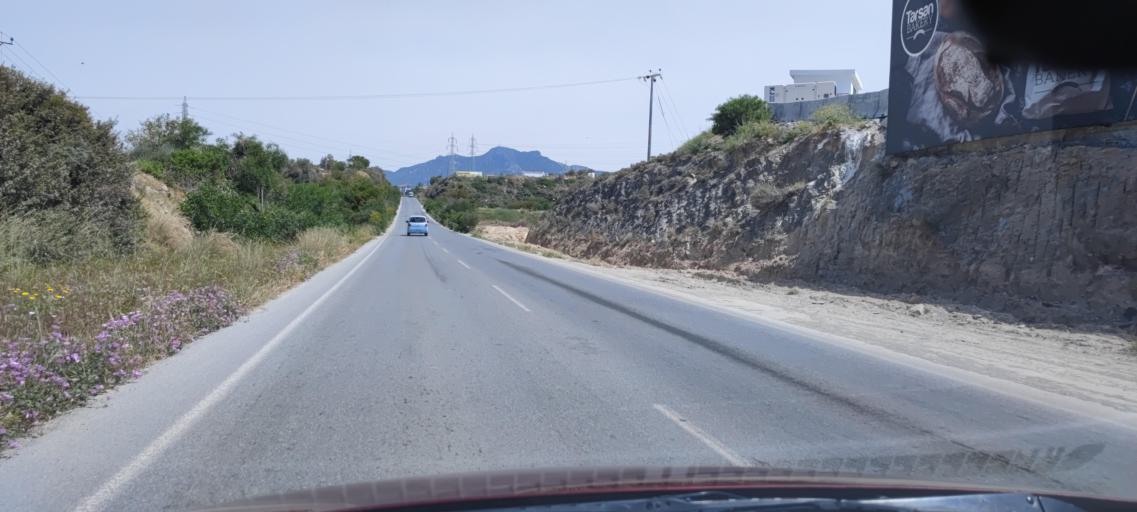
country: CY
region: Keryneia
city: Kyrenia
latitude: 35.3325
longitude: 33.4537
